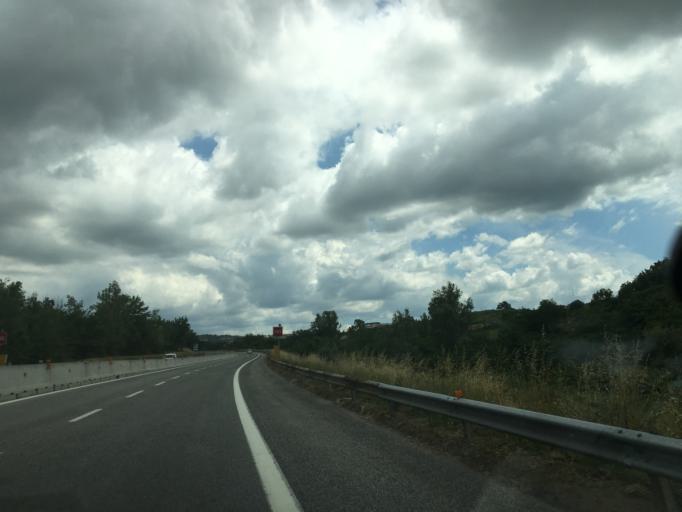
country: IT
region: Campania
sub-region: Provincia di Avellino
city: Passo di Mirabella-Pianopantano
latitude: 41.0667
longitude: 15.0061
